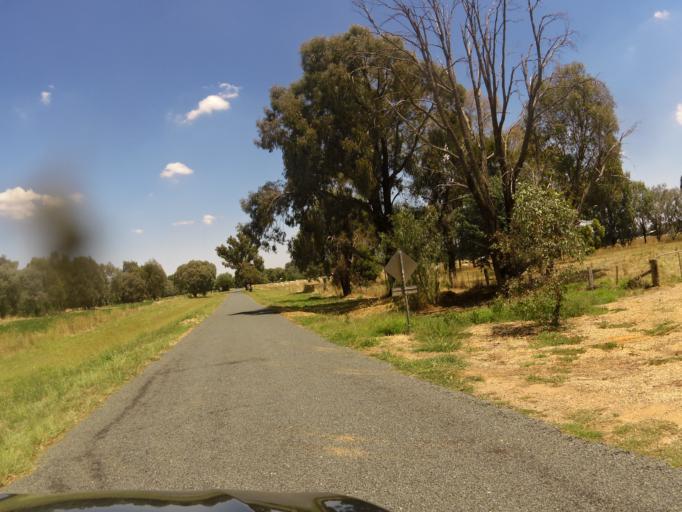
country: AU
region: Victoria
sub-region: Wangaratta
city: Wangaratta
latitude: -36.4294
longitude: 146.5502
